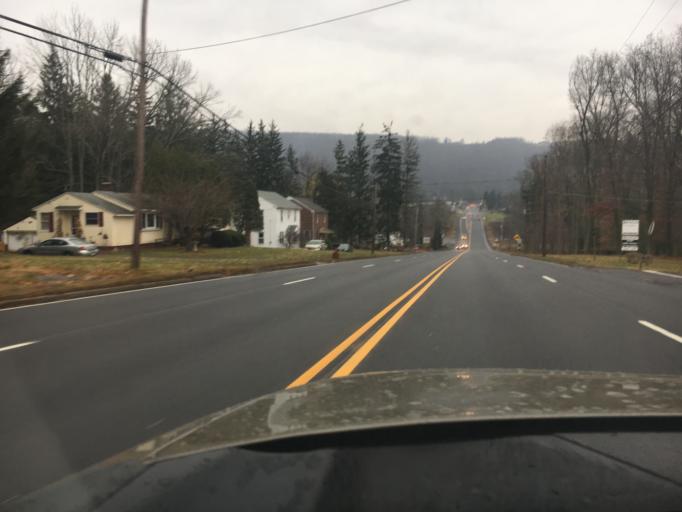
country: US
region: Pennsylvania
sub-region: Luzerne County
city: Harleigh
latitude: 41.0158
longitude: -75.9649
